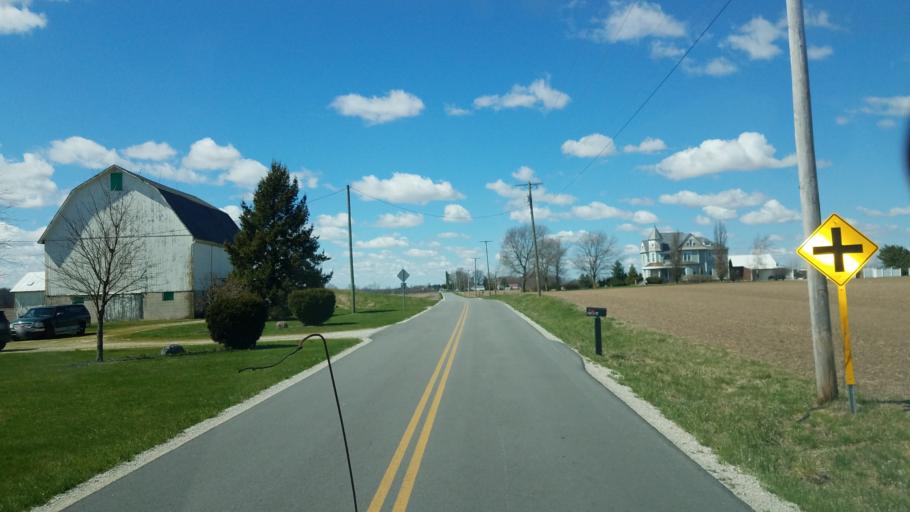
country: US
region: Ohio
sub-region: Seneca County
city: Fostoria
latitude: 41.1578
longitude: -83.4631
